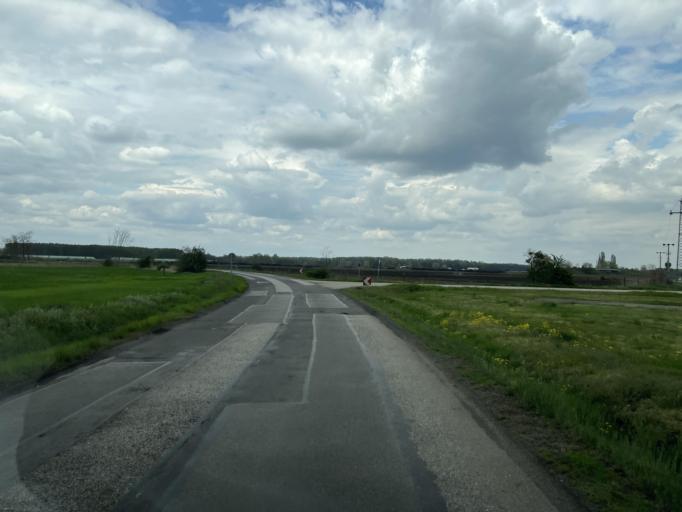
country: HU
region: Pest
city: Hernad
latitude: 47.1842
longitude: 19.4267
